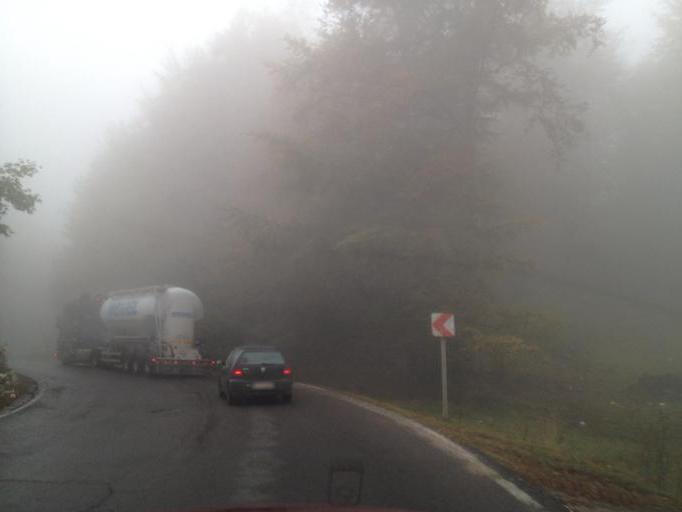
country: RO
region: Arges
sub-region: Comuna Dambovicioara
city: Dambovicioara
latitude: 45.4209
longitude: 25.2482
